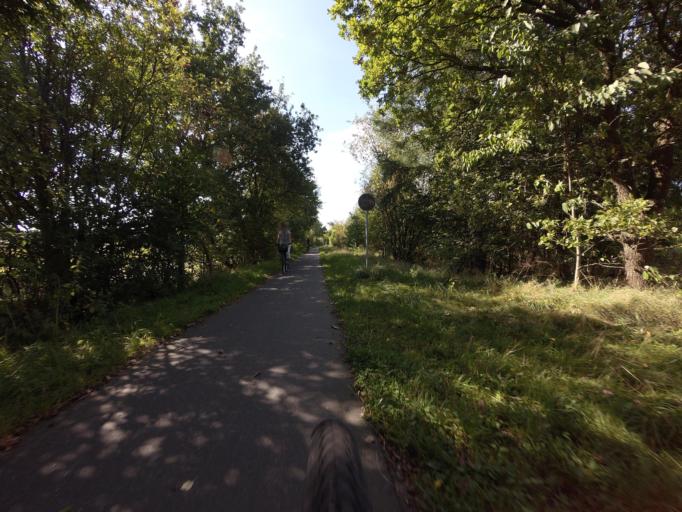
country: DK
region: Central Jutland
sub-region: Viborg Kommune
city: Viborg
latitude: 56.4195
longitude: 9.3772
